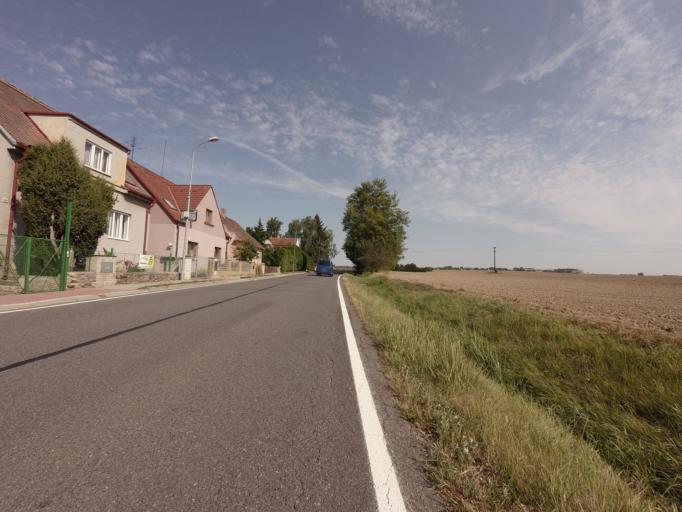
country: CZ
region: Jihocesky
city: Bernartice
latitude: 49.3723
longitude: 14.3794
